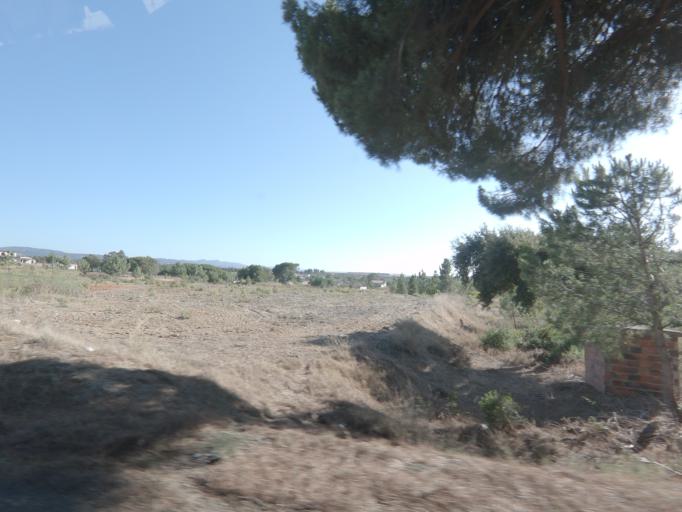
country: PT
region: Setubal
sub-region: Moita
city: Moita
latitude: 38.6270
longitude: -8.9618
